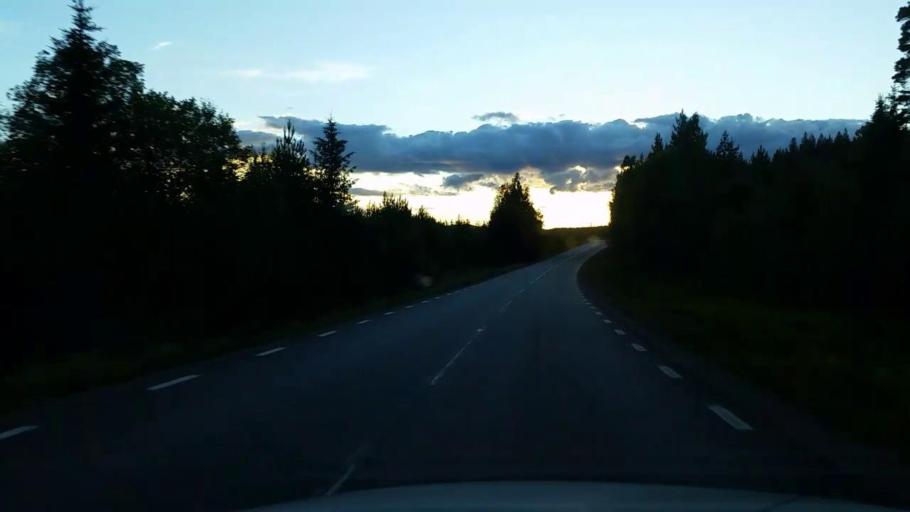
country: SE
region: Gaevleborg
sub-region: Ljusdals Kommun
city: Farila
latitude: 62.1019
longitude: 15.7797
